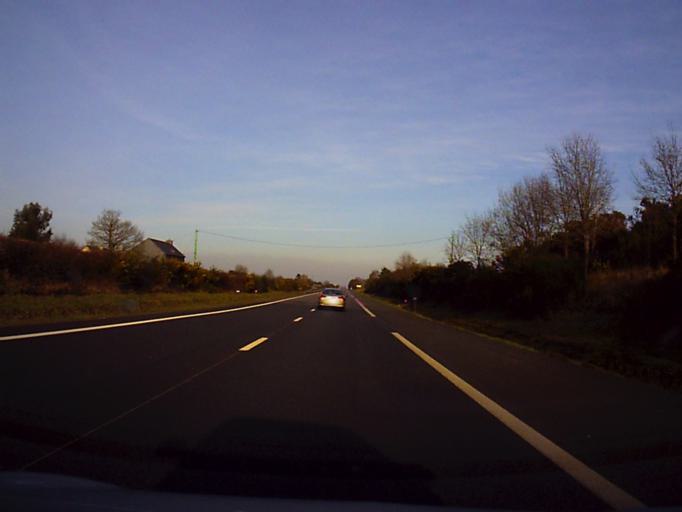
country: FR
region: Brittany
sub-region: Departement d'Ille-et-Vilaine
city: Monterfil
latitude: 48.0372
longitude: -1.9686
